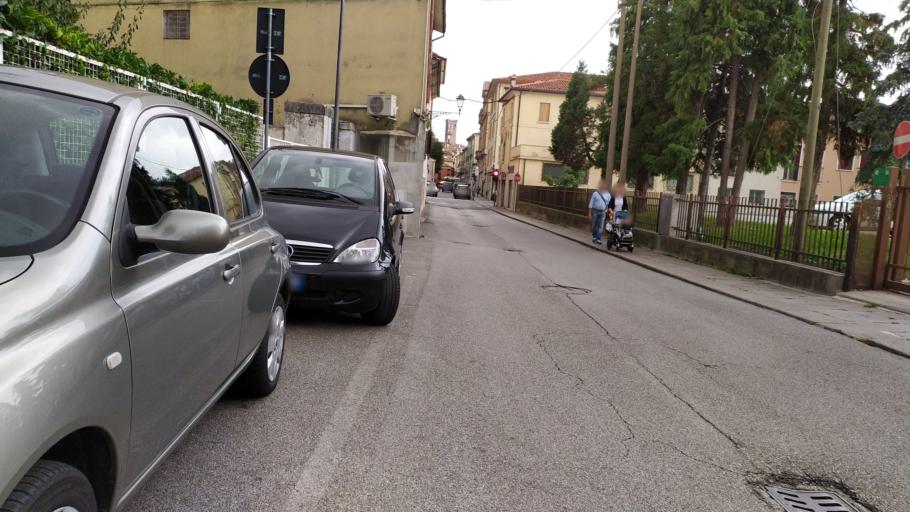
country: IT
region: Veneto
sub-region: Provincia di Vicenza
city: Bassano del Grappa
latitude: 45.7677
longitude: 11.7267
